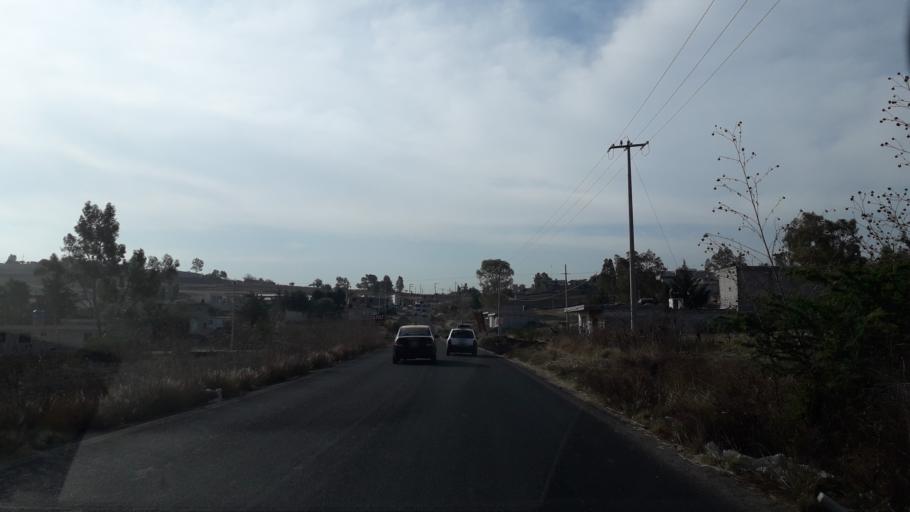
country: MX
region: Puebla
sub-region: Puebla
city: San Andres Azumiatla
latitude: 18.9152
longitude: -98.2450
